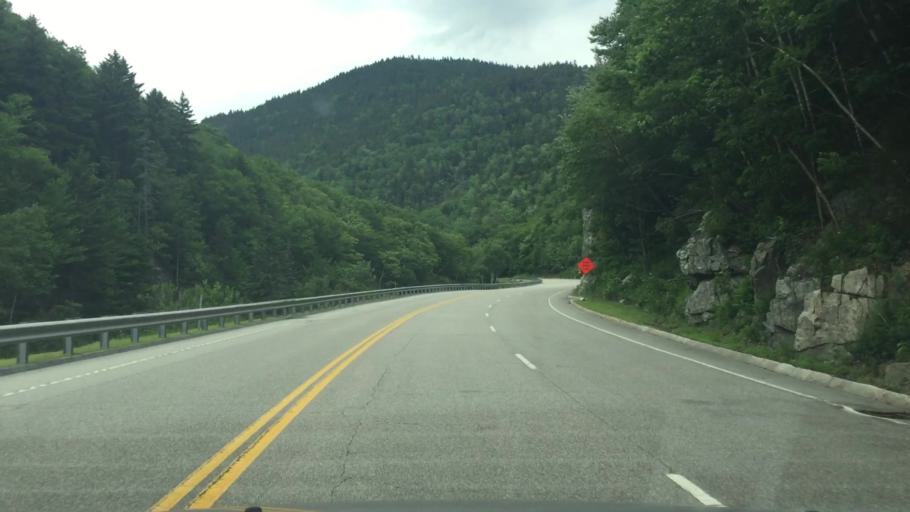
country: US
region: New Hampshire
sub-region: Grafton County
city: Deerfield
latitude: 44.2024
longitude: -71.4050
